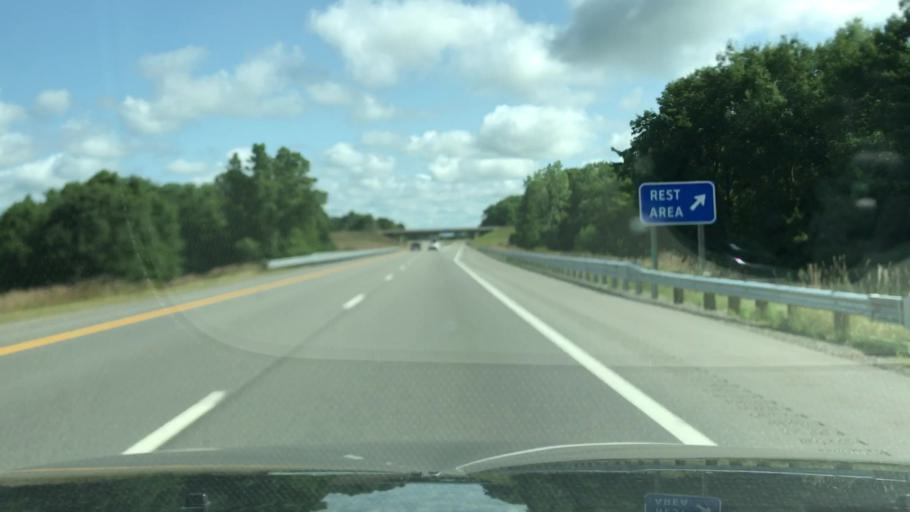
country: US
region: Michigan
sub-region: Montcalm County
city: Howard City
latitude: 43.4540
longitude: -85.4823
